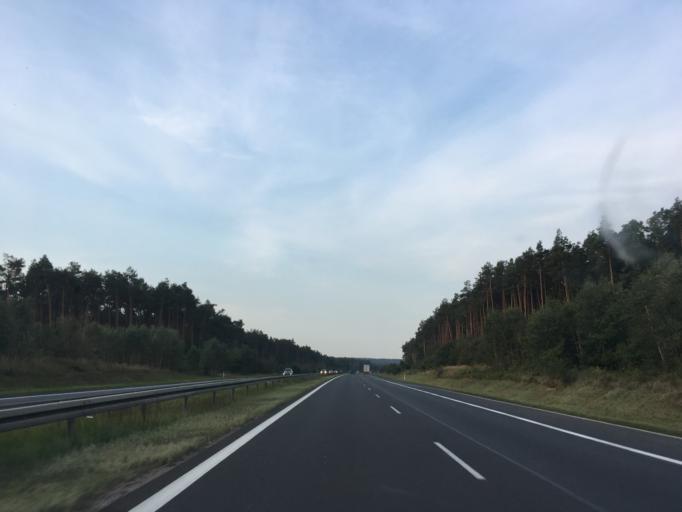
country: PL
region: Lodz Voivodeship
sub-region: Powiat radomszczanski
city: Gomunice
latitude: 51.1676
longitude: 19.4597
